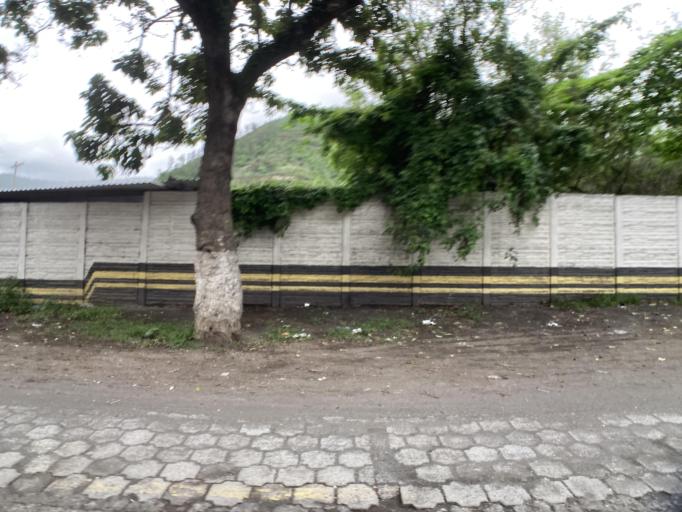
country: GT
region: Sacatepequez
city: Jocotenango
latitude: 14.5832
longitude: -90.7468
